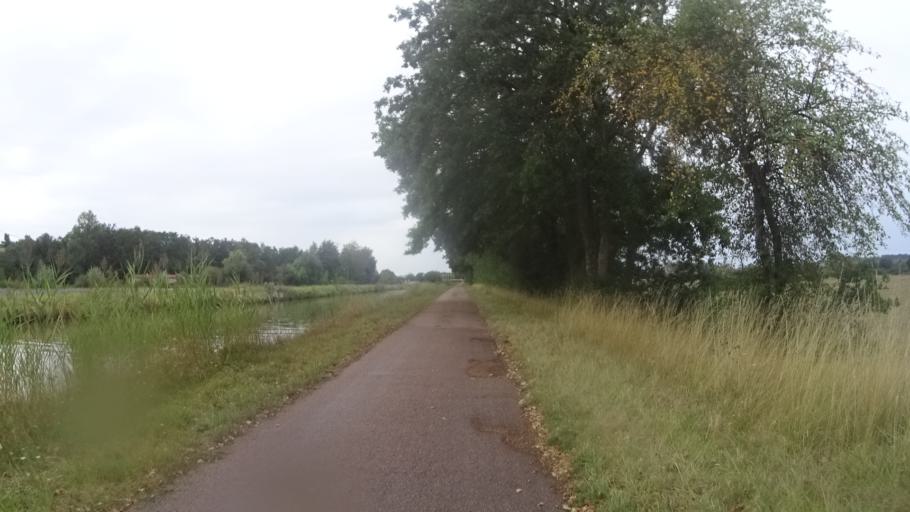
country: FR
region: Bourgogne
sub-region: Departement de la Nievre
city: Saint-Leger-des-Vignes
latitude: 46.8164
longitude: 3.3622
